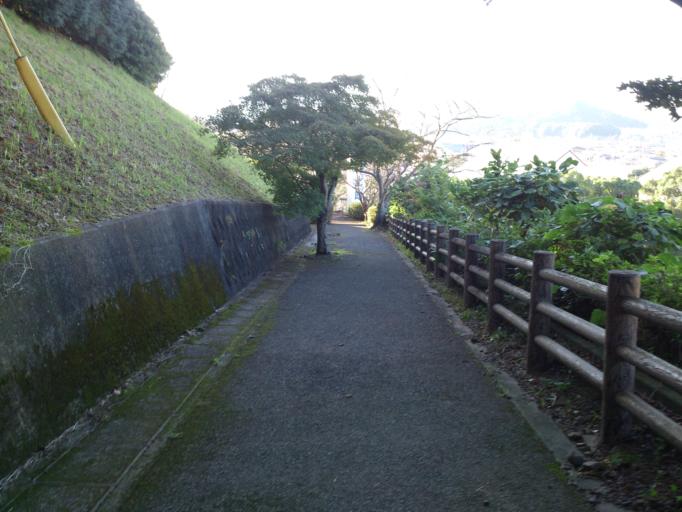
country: JP
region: Saga Prefecture
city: Imaricho-ko
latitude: 33.1803
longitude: 129.8807
